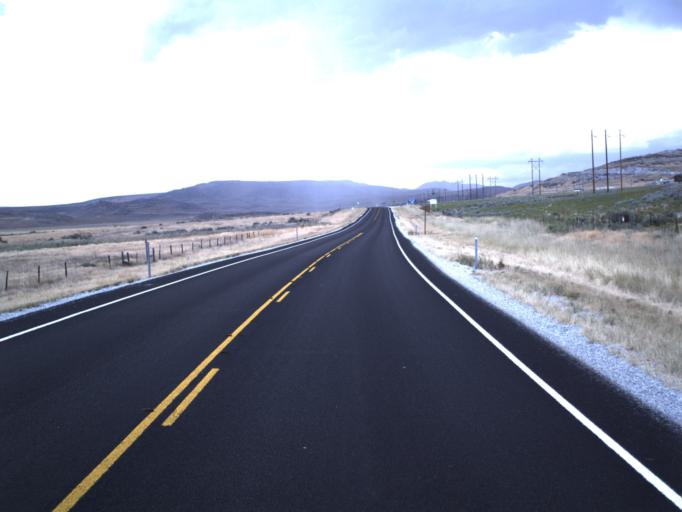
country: US
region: Utah
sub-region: Box Elder County
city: Tremonton
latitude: 41.6320
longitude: -112.4196
